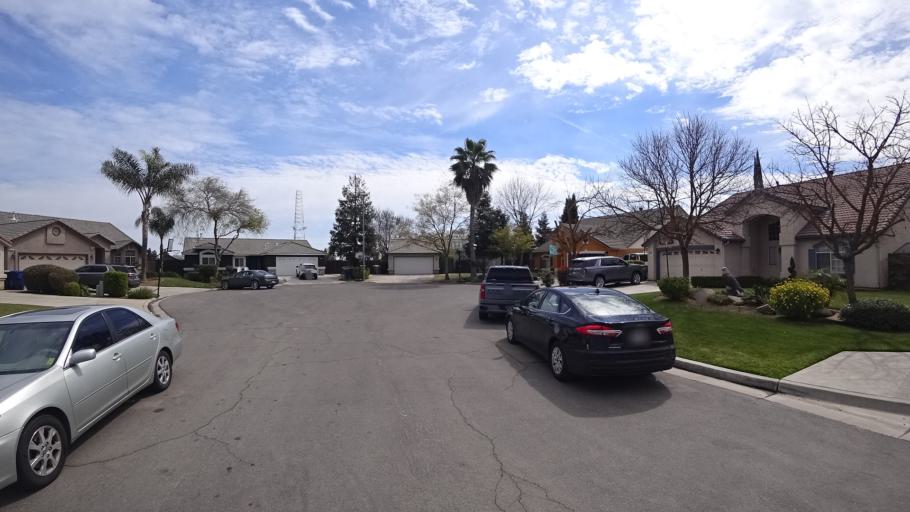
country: US
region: California
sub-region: Fresno County
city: West Park
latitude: 36.8173
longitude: -119.8856
